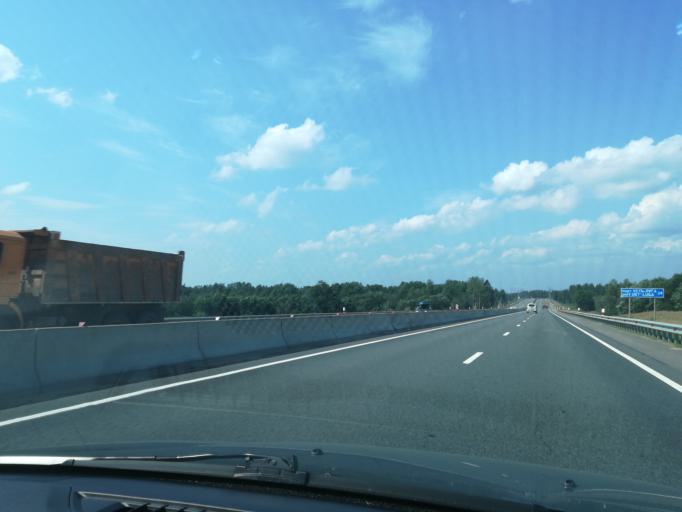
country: RU
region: Leningrad
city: Kingisepp
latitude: 59.5955
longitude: 28.7343
